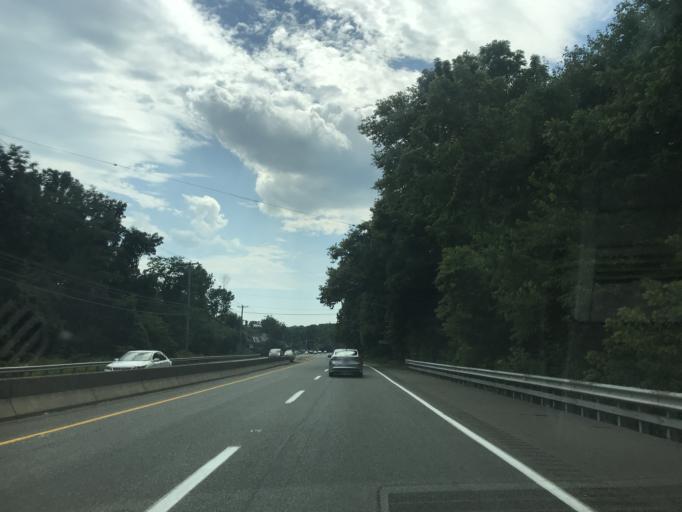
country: US
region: Pennsylvania
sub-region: Chester County
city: West Chester
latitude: 39.8731
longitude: -75.5863
